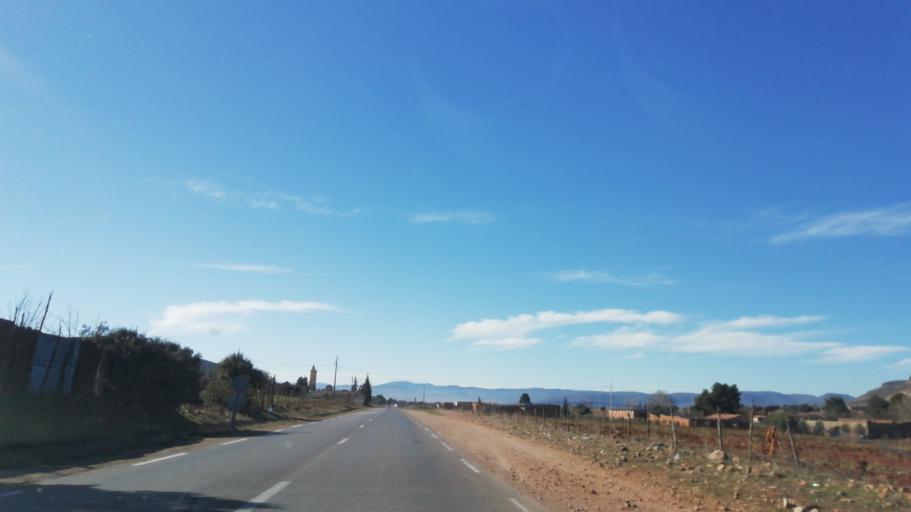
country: DZ
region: Tlemcen
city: Sebdou
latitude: 34.6919
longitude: -1.2408
